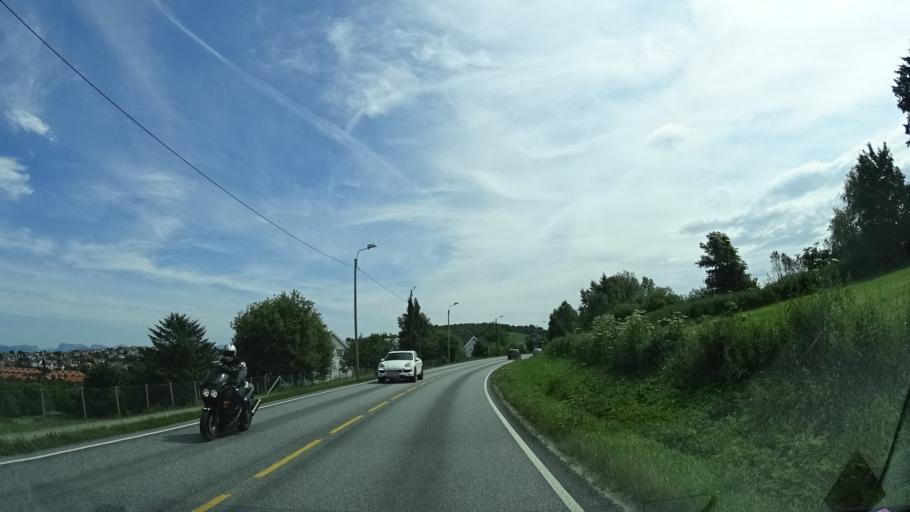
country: NO
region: Rogaland
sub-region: Randaberg
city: Randaberg
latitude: 58.9891
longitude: 5.6620
